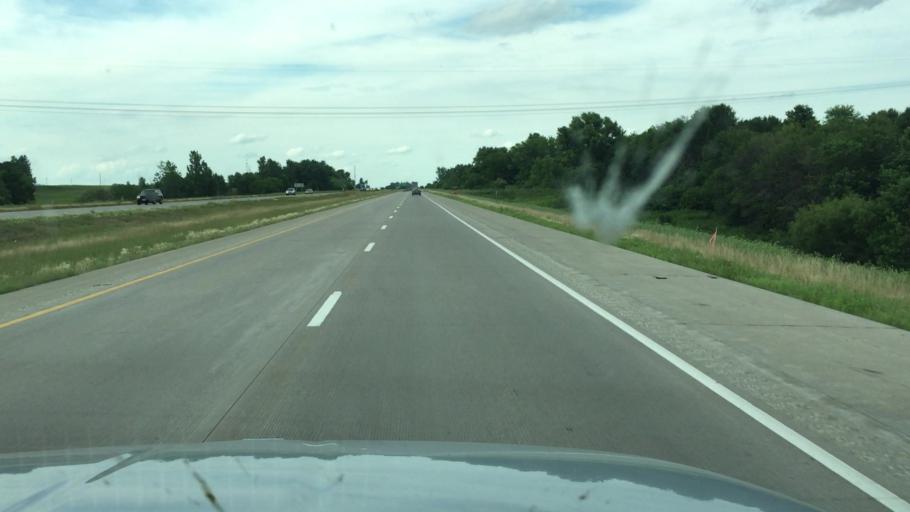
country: US
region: Iowa
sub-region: Scott County
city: Walcott
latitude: 41.5734
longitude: -90.6777
